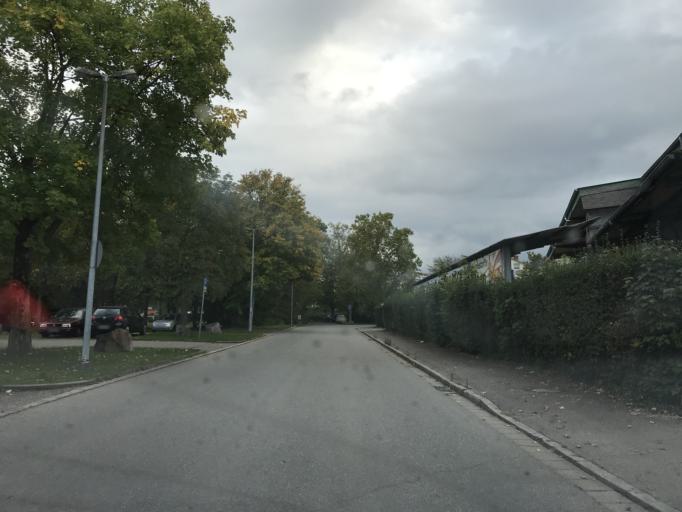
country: DE
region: Baden-Wuerttemberg
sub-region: Freiburg Region
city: Loerrach
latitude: 47.6258
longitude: 7.6607
